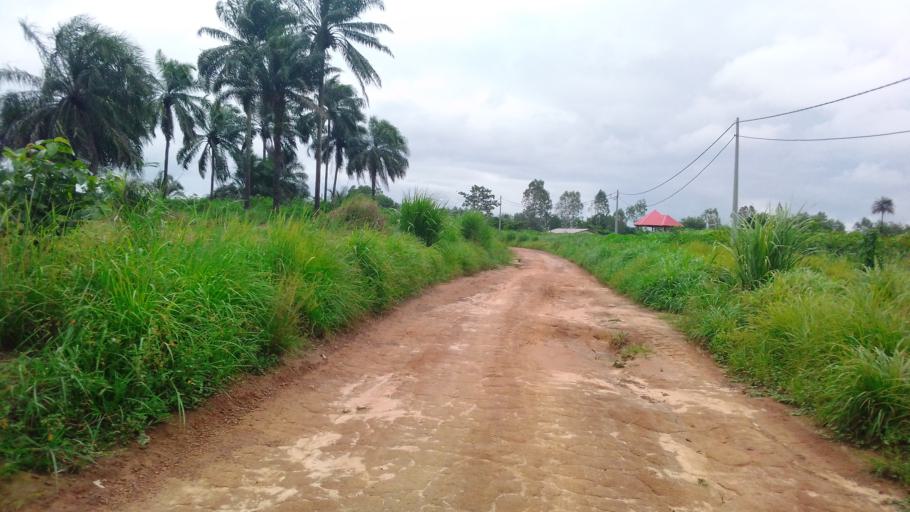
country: SL
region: Northern Province
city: Lunsar
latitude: 8.6932
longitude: -12.5491
